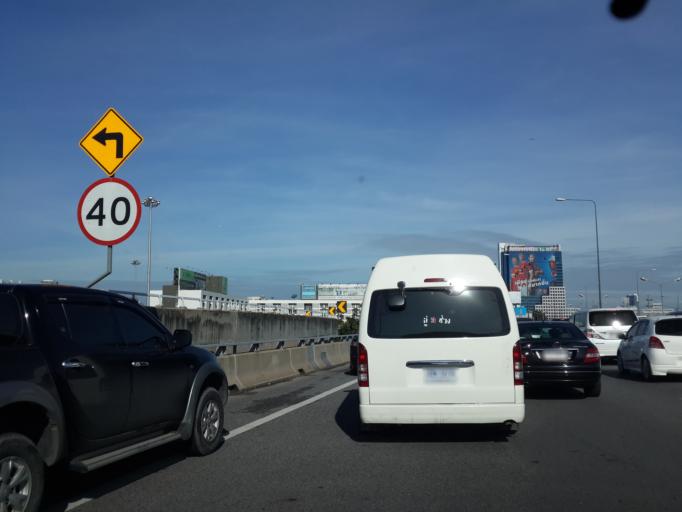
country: TH
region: Bangkok
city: Watthana
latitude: 13.7513
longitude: 100.5930
